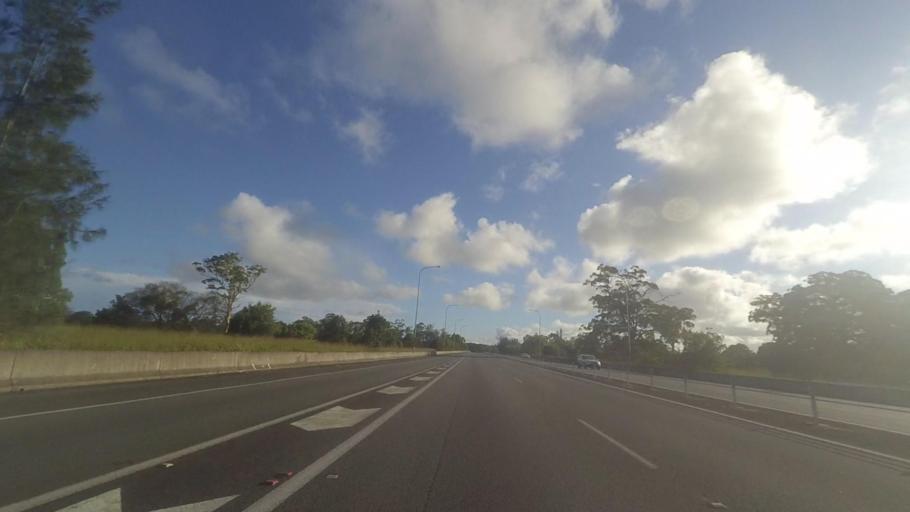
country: AU
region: New South Wales
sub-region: Great Lakes
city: Nabiac
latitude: -32.1017
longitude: 152.3752
